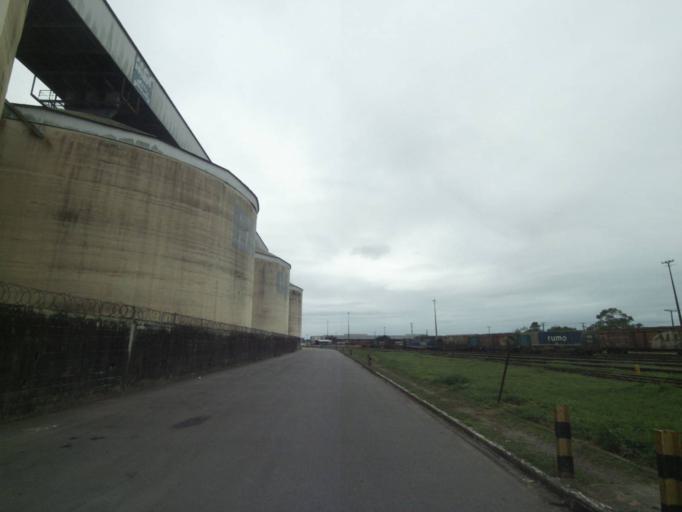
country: BR
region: Parana
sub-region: Paranagua
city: Paranagua
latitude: -25.5413
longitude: -48.5409
